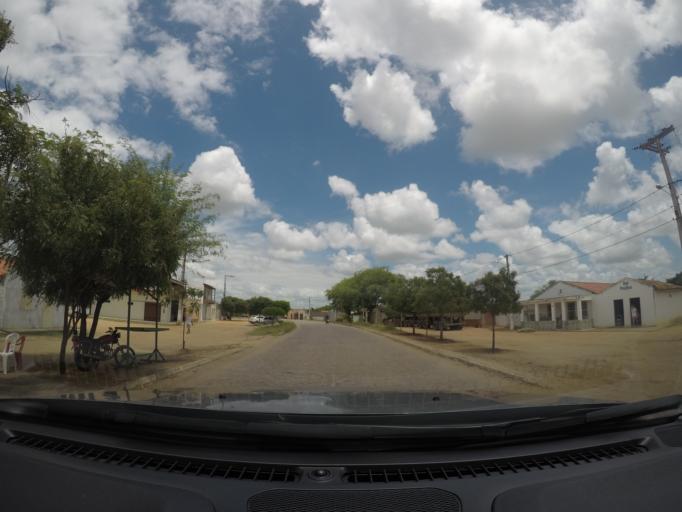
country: BR
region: Bahia
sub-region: Itaberaba
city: Itaberaba
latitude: -12.3620
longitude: -40.0398
